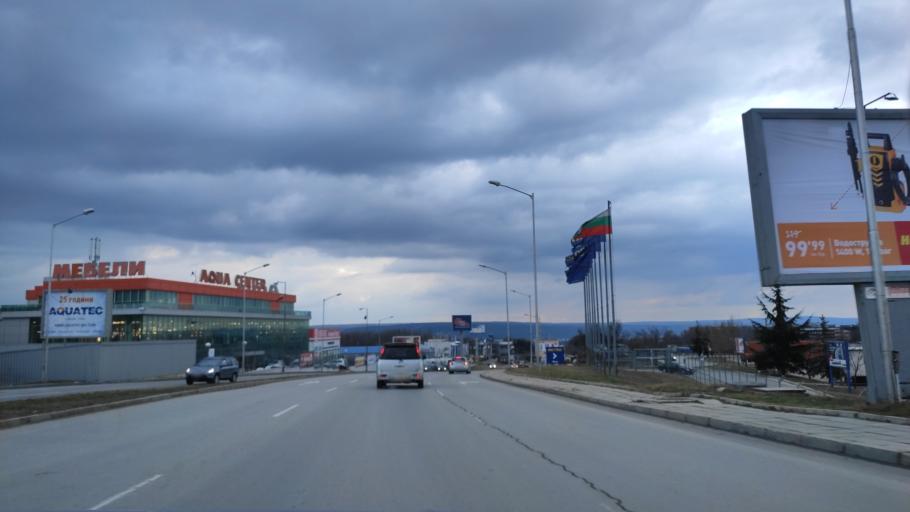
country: BG
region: Varna
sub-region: Obshtina Aksakovo
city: Aksakovo
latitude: 43.2326
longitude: 27.8638
